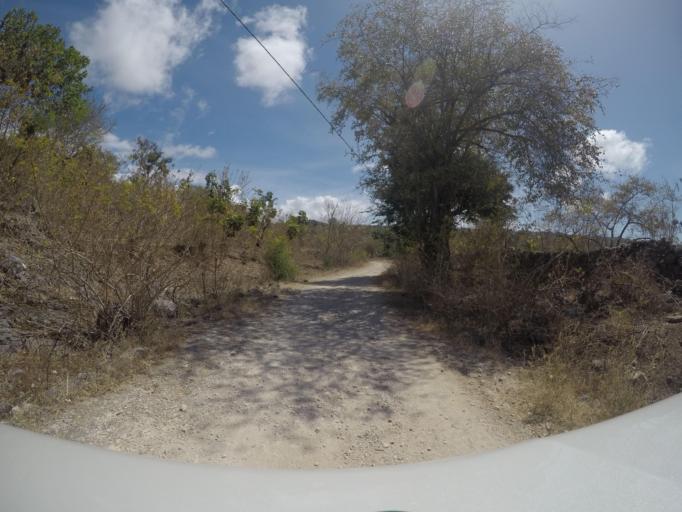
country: TL
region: Baucau
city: Baucau
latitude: -8.4446
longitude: 126.4386
